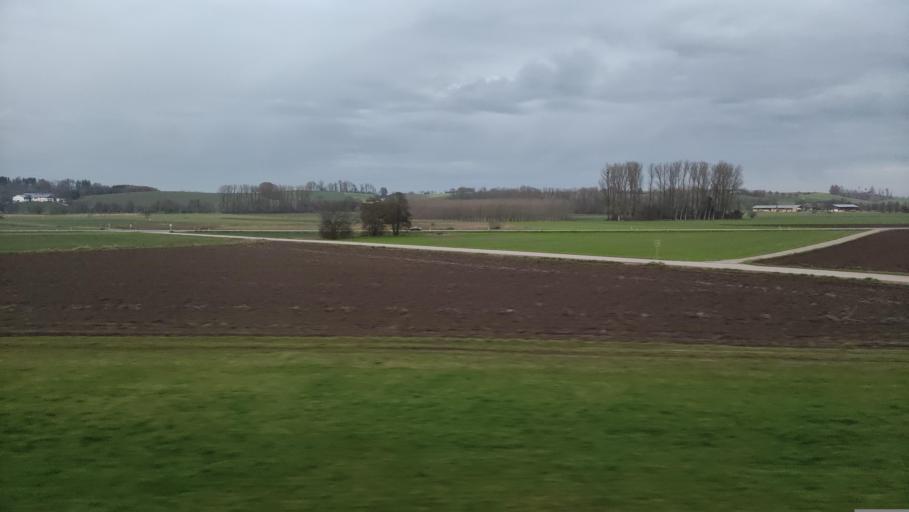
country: DE
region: Bavaria
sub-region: Upper Bavaria
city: Rattenkirchen
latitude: 48.2574
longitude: 12.3402
